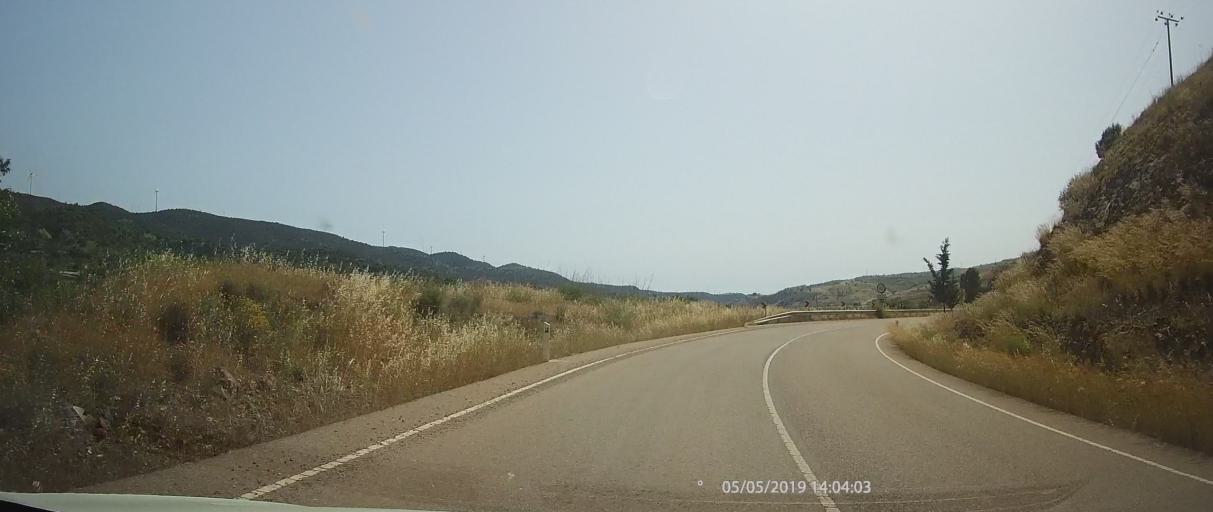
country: CY
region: Limassol
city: Pissouri
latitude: 34.7618
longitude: 32.6293
